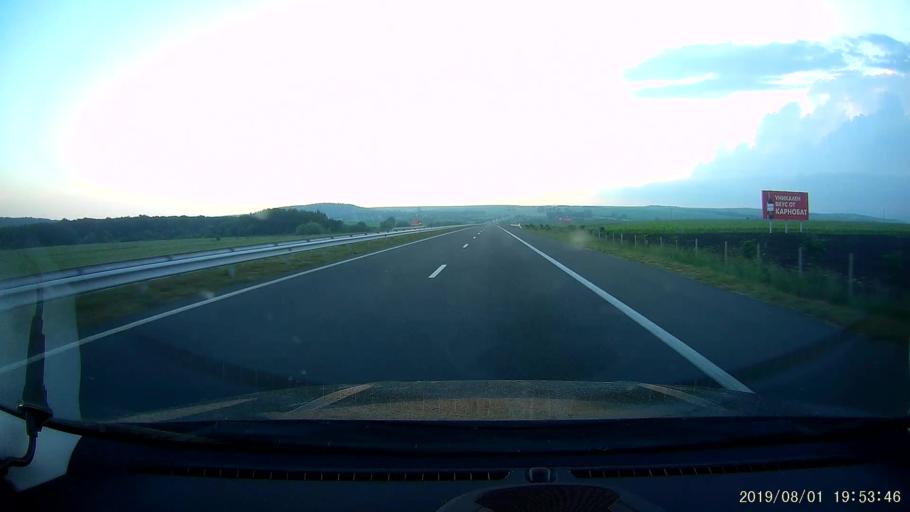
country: BG
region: Burgas
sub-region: Obshtina Karnobat
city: Karnobat
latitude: 42.5813
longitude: 26.9216
